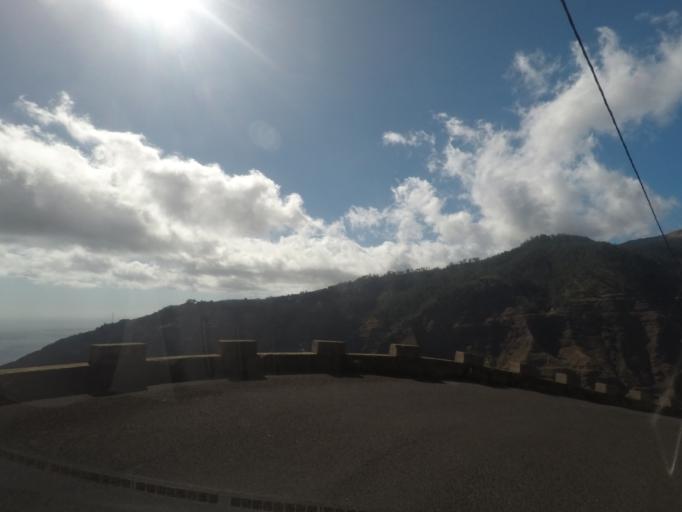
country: PT
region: Madeira
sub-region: Ribeira Brava
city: Campanario
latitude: 32.6920
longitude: -17.0388
